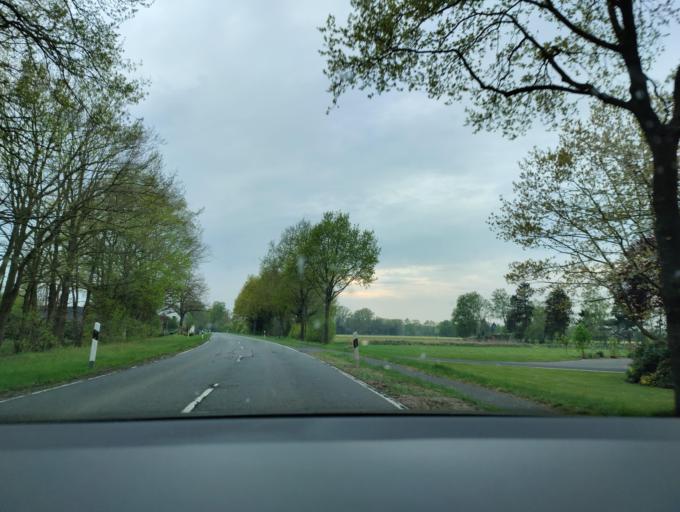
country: DE
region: Lower Saxony
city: Wietmarschen
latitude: 52.5105
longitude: 7.1540
